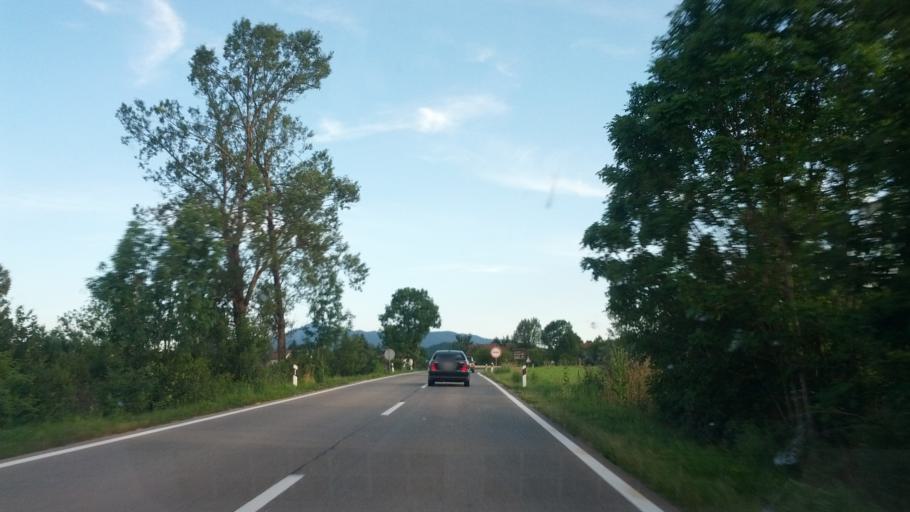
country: BA
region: Federation of Bosnia and Herzegovina
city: Izacic
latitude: 44.9106
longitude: 15.7191
